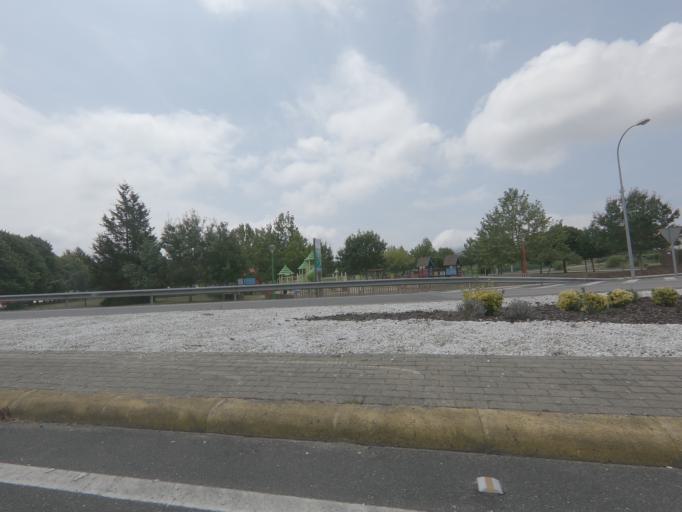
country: ES
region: Galicia
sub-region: Provincia de Pontevedra
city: O Rosal
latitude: 41.9148
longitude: -8.8290
